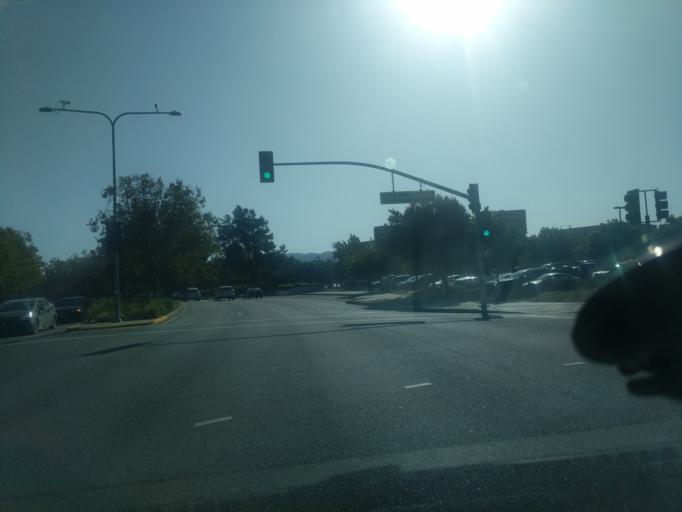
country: US
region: California
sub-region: Alameda County
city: Pleasanton
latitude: 37.6946
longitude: -121.8783
